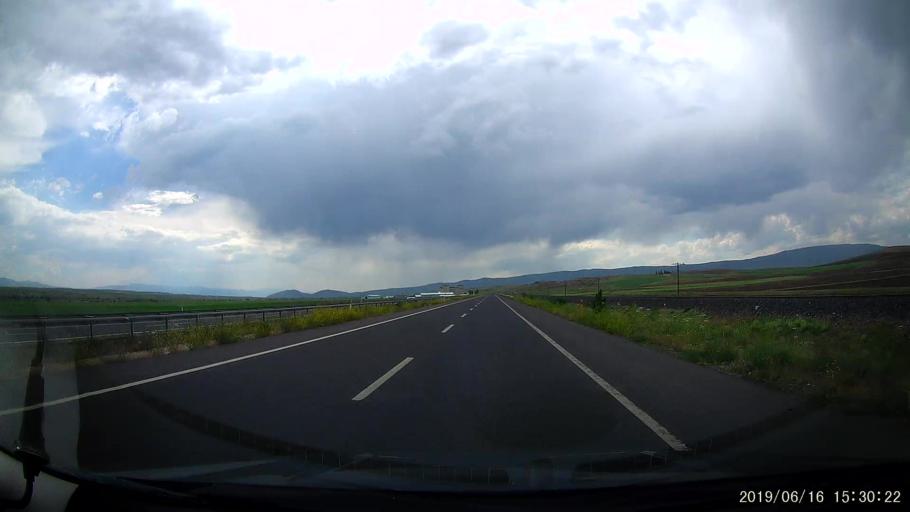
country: TR
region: Erzurum
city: Horasan
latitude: 40.0336
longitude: 42.1076
